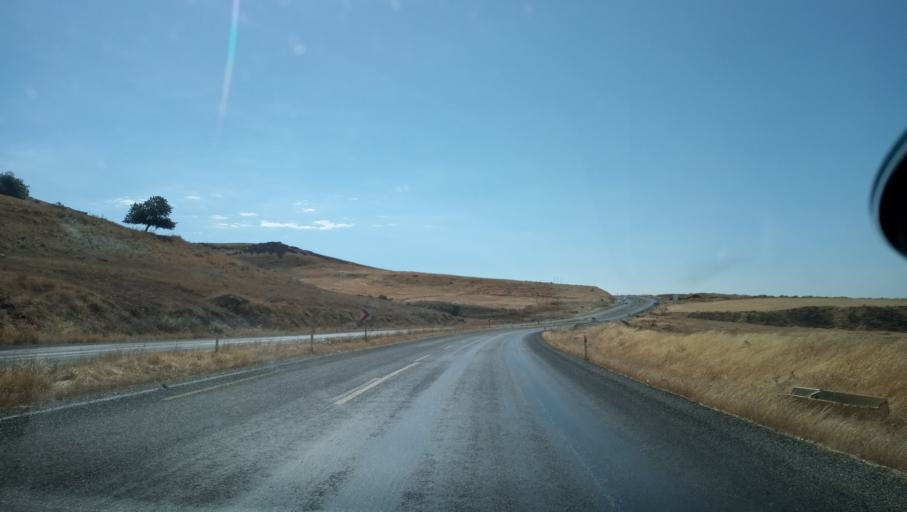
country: TR
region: Diyarbakir
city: Silvan
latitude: 38.1320
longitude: 41.0497
